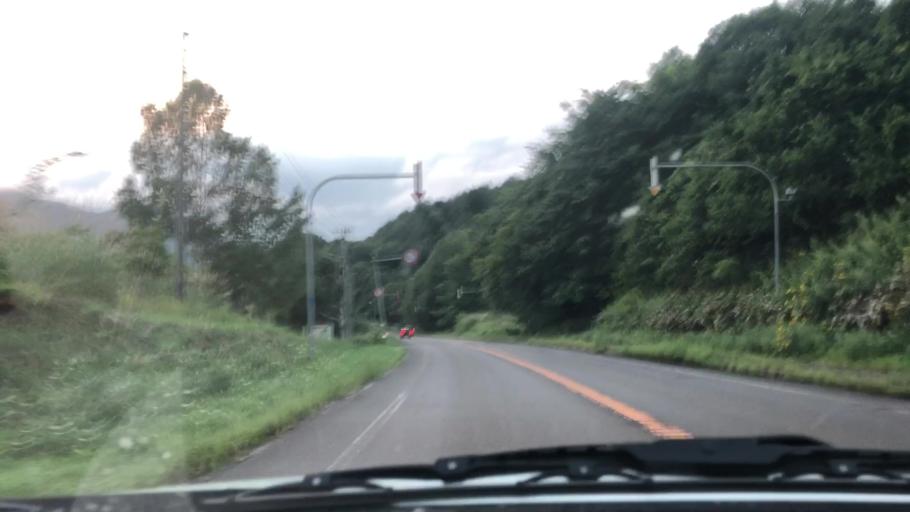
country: JP
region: Hokkaido
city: Iwamizawa
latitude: 42.9354
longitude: 142.0526
